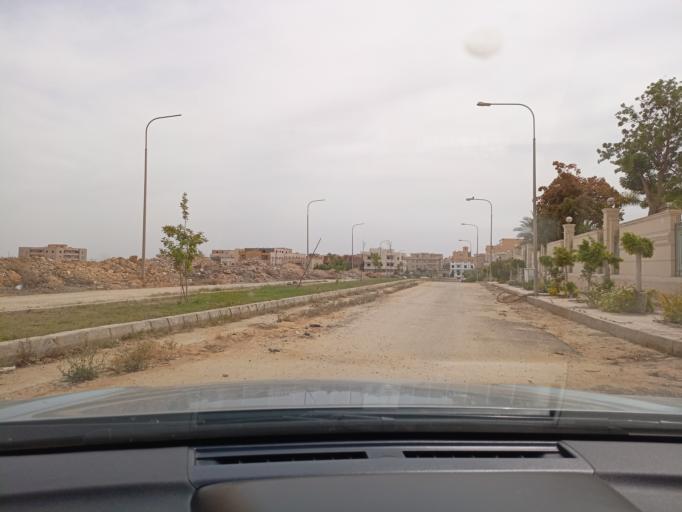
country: EG
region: Muhafazat al Qalyubiyah
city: Al Khankah
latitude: 30.2487
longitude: 31.5054
